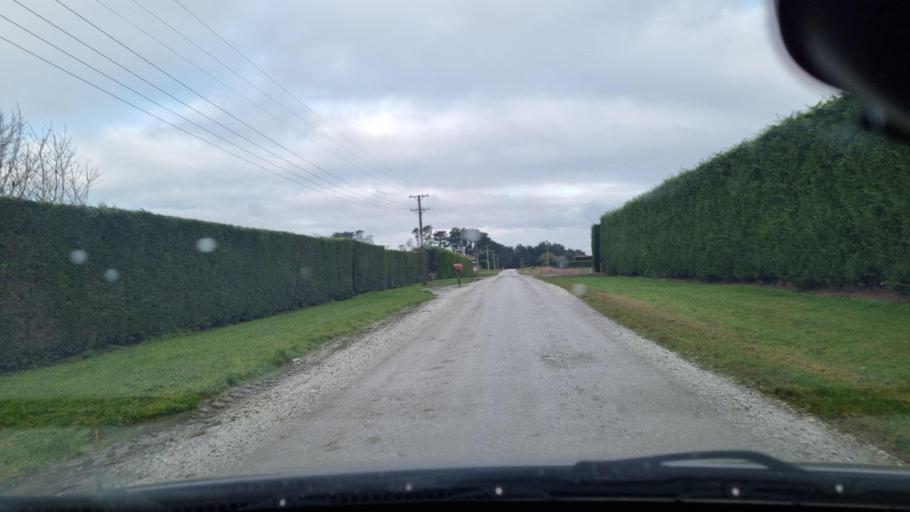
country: NZ
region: Southland
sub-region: Invercargill City
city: Invercargill
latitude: -46.4148
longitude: 168.4421
